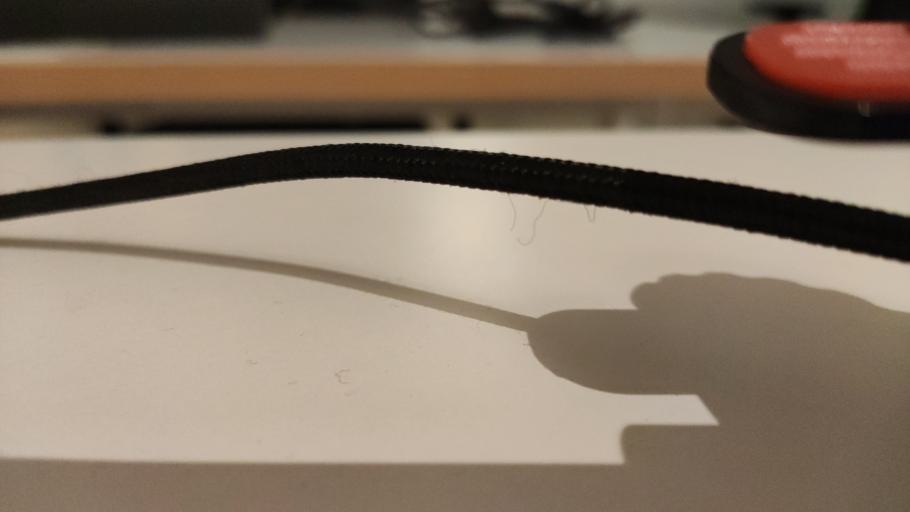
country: RU
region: Moskovskaya
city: Orekhovo-Zuyevo
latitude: 55.8335
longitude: 38.9678
